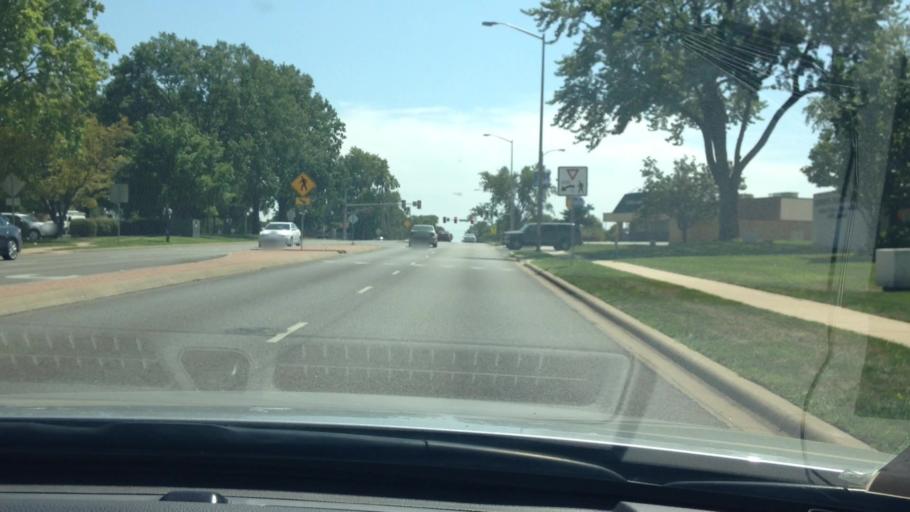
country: US
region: Kansas
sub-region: Johnson County
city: Overland Park
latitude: 38.9747
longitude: -94.6864
